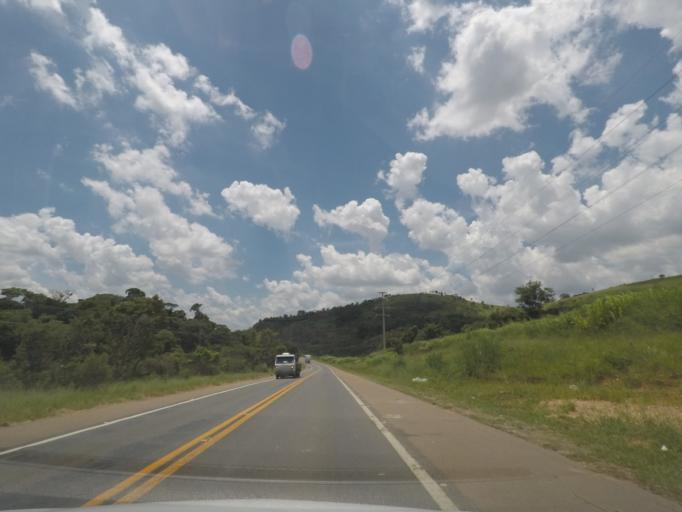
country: BR
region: Sao Paulo
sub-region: Vinhedo
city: Vinhedo
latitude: -23.0606
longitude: -47.0278
